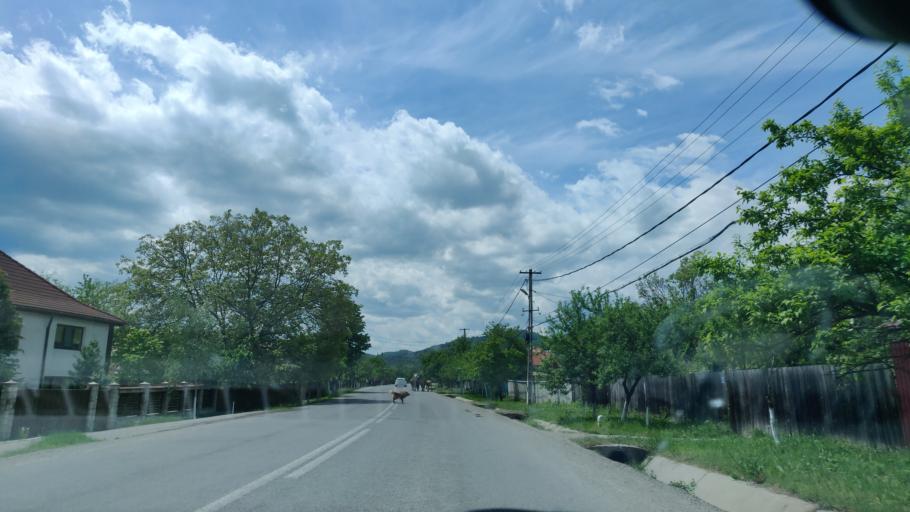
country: RO
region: Vrancea
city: Matacina
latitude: 45.8906
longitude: 26.8348
